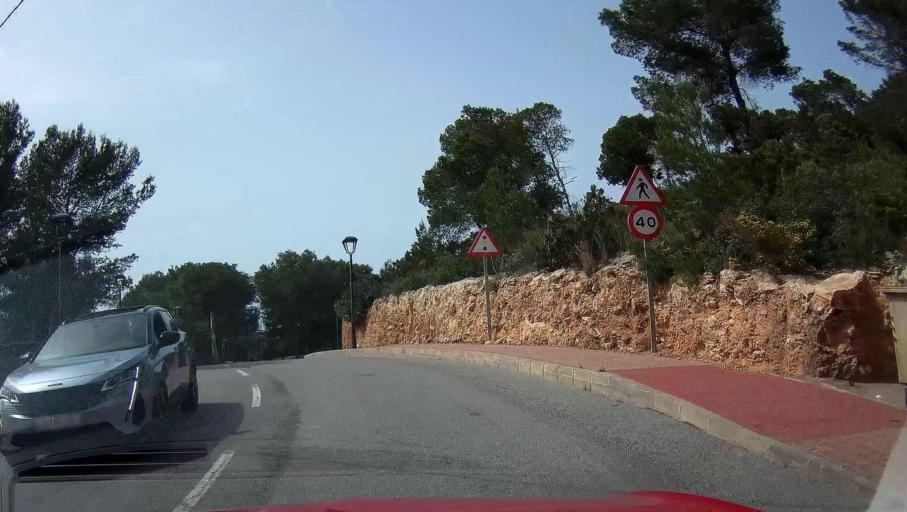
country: ES
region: Balearic Islands
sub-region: Illes Balears
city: Sant Joan de Labritja
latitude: 39.1087
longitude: 1.5197
